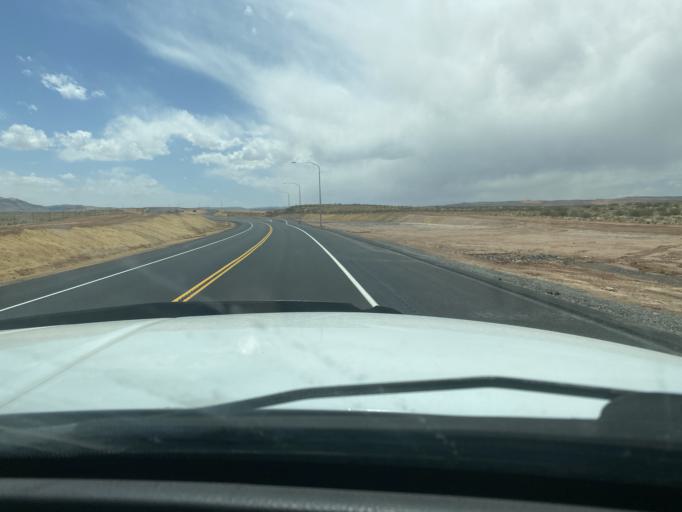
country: US
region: Utah
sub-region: Washington County
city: Hurricane
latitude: 37.1355
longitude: -113.3479
